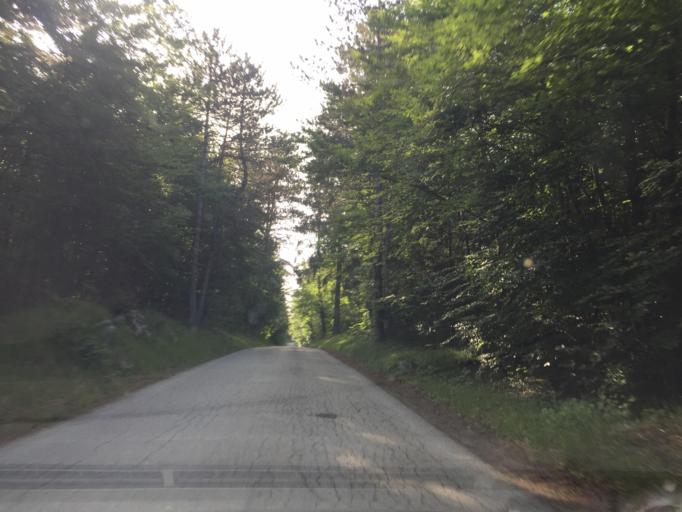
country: HR
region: Istarska
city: Buzet
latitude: 45.4760
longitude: 14.0790
